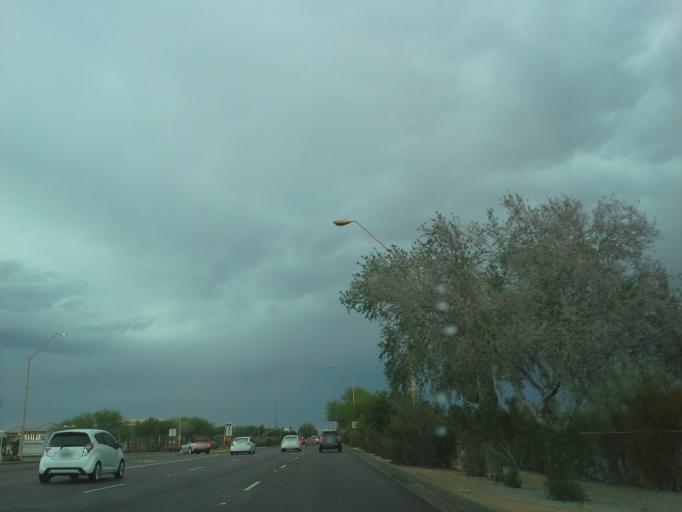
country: US
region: Arizona
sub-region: Maricopa County
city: Paradise Valley
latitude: 33.6367
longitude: -111.9178
